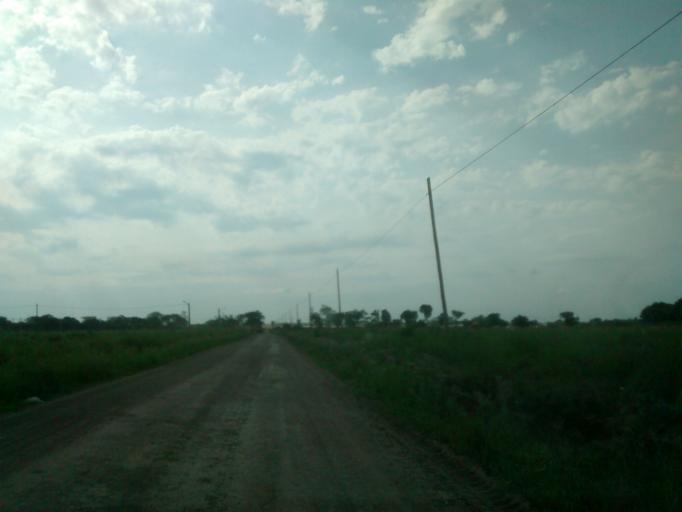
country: AR
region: Chaco
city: Fontana
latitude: -27.4052
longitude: -58.9758
